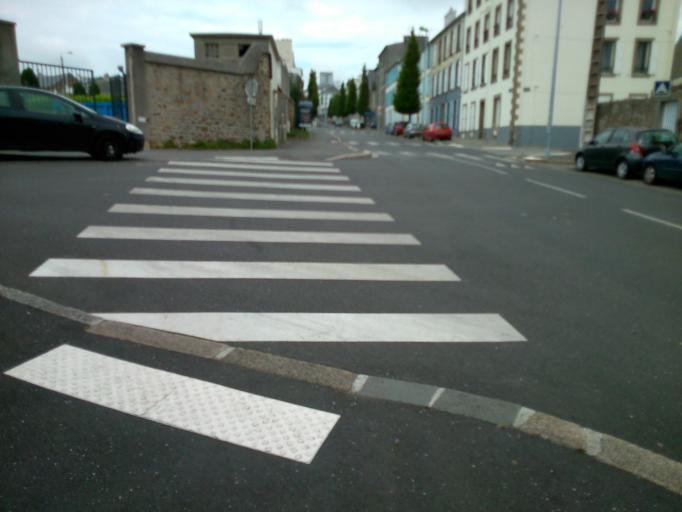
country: FR
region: Brittany
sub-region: Departement du Finistere
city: Brest
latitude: 48.3938
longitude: -4.4747
